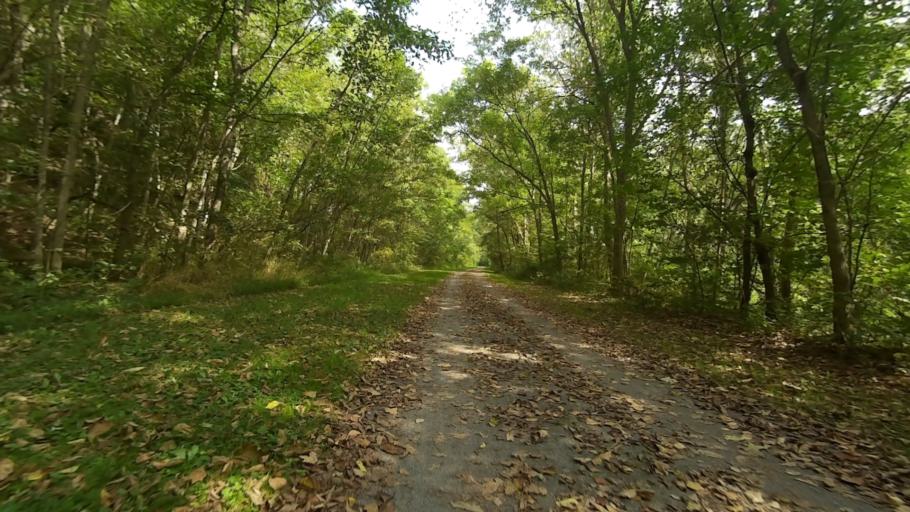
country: US
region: Pennsylvania
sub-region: Blair County
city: Williamsburg
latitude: 40.5013
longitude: -78.1664
